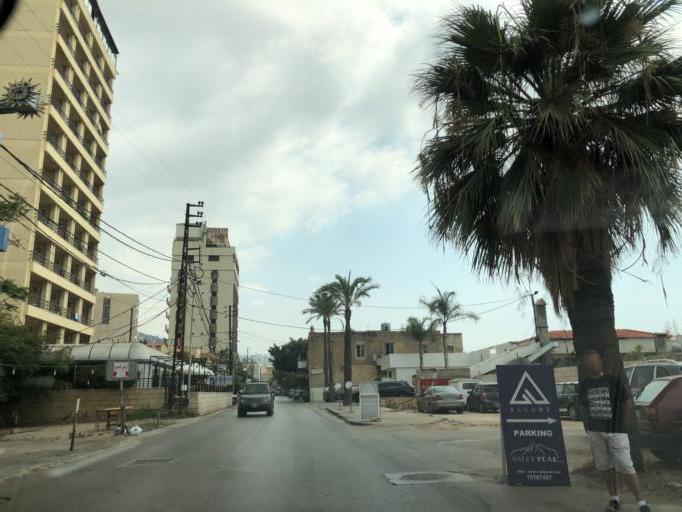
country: LB
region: Mont-Liban
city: Djounie
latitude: 33.9929
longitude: 35.6398
